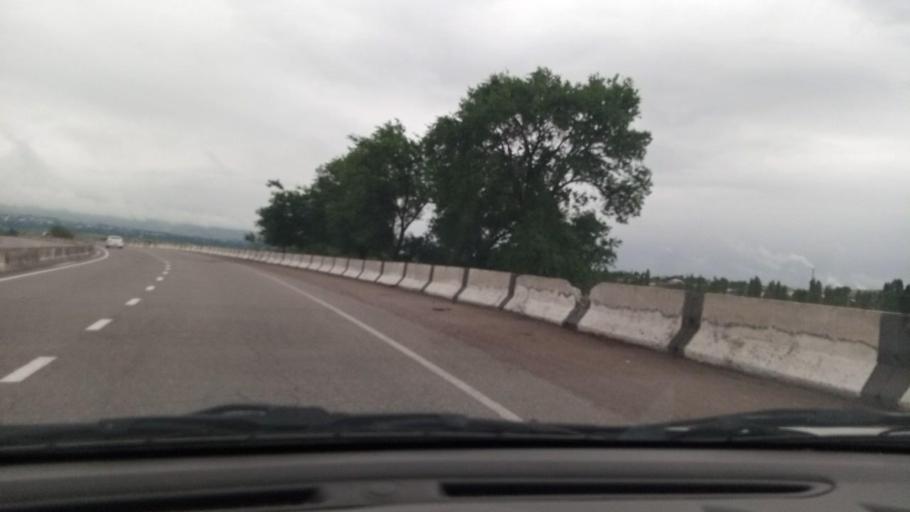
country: UZ
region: Toshkent
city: Angren
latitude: 40.9464
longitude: 69.9076
